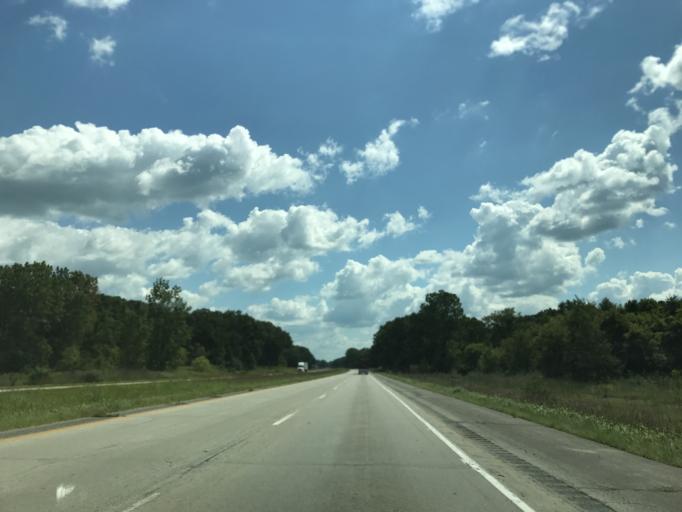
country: US
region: Indiana
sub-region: Starke County
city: Koontz Lake
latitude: 41.3675
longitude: -86.4828
